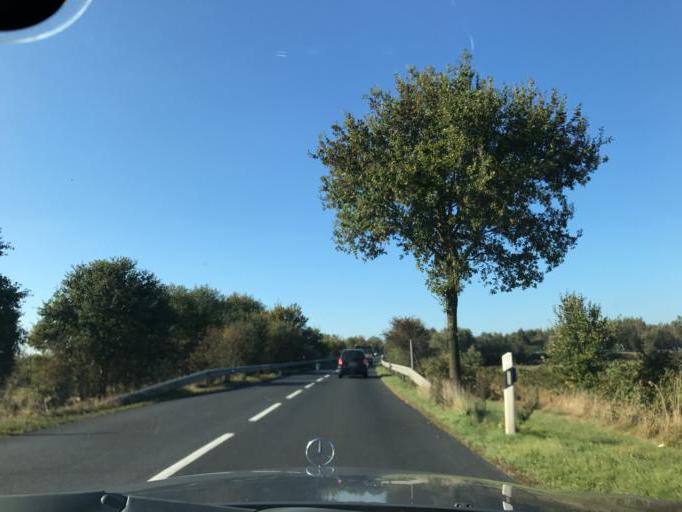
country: DE
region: Lower Saxony
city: Bunde
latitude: 53.1366
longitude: 7.2779
